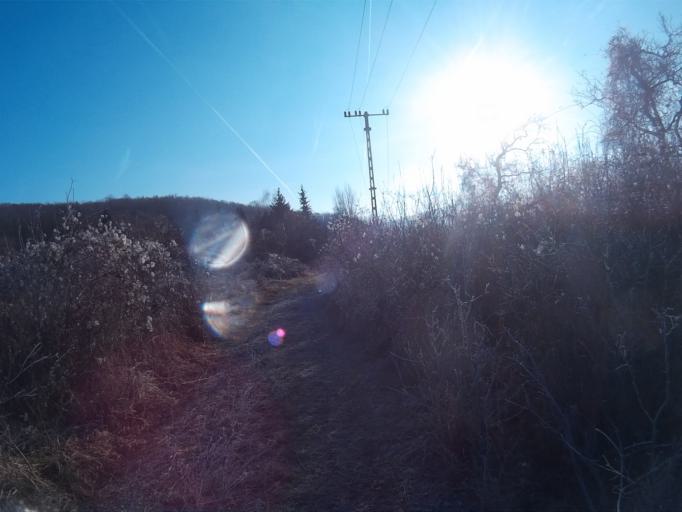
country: HU
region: Nograd
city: Bercel
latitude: 47.9116
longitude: 19.3960
